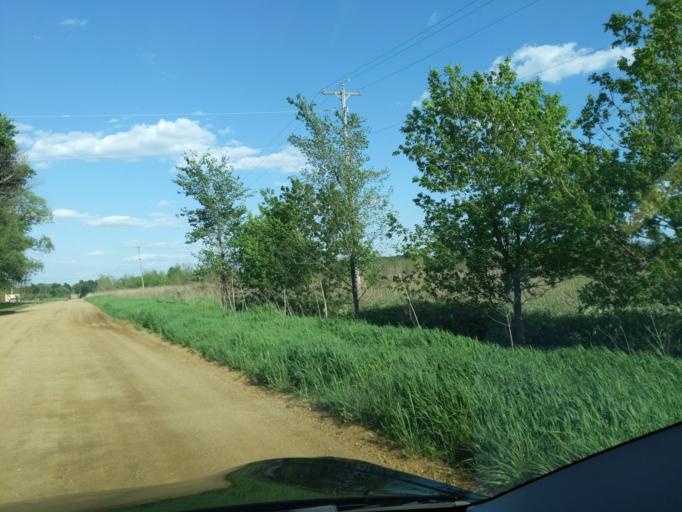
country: US
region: Michigan
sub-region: Eaton County
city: Potterville
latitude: 42.6828
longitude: -84.7301
